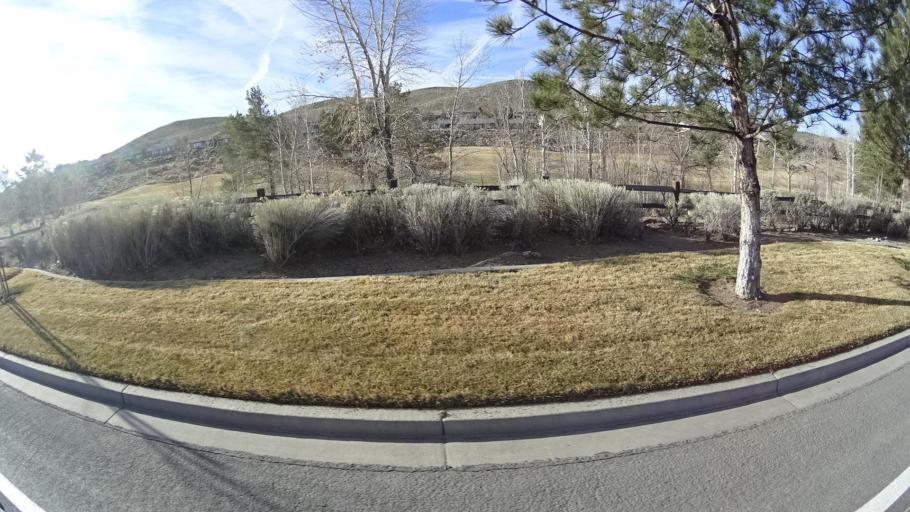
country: US
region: Nevada
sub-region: Washoe County
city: Spanish Springs
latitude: 39.6070
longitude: -119.6834
